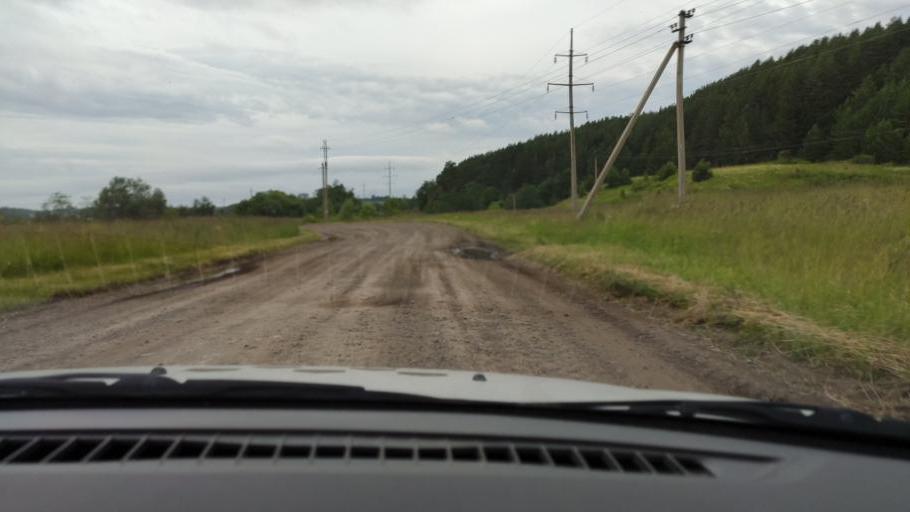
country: RU
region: Perm
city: Orda
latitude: 57.3019
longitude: 56.6310
